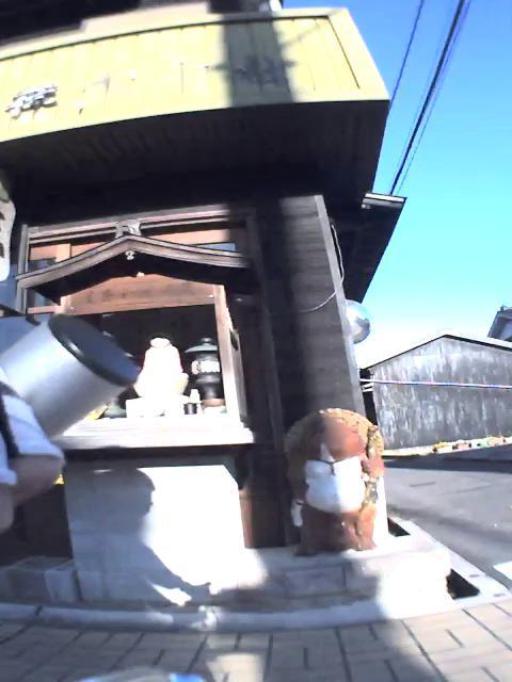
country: JP
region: Yamaguchi
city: Nagato
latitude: 34.3931
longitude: 131.1983
